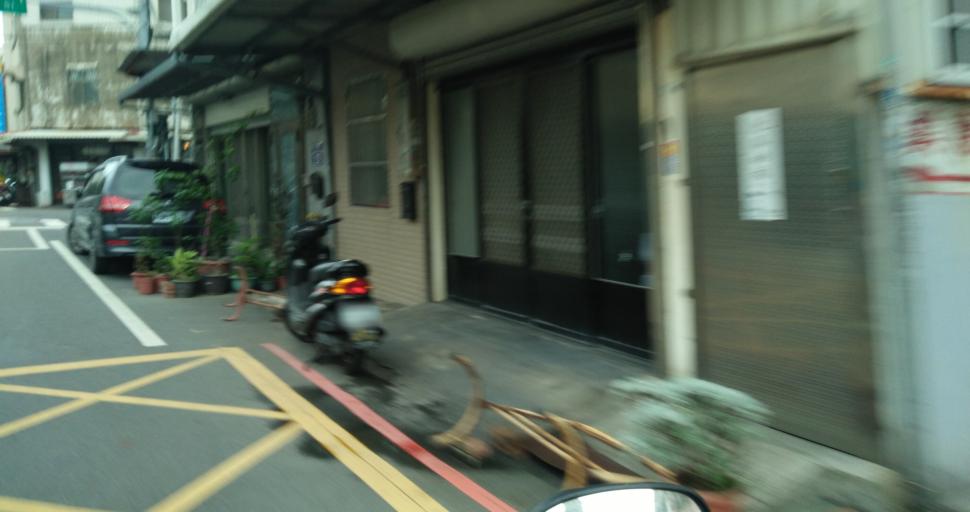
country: TW
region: Taiwan
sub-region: Hsinchu
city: Hsinchu
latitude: 24.8029
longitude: 120.9570
